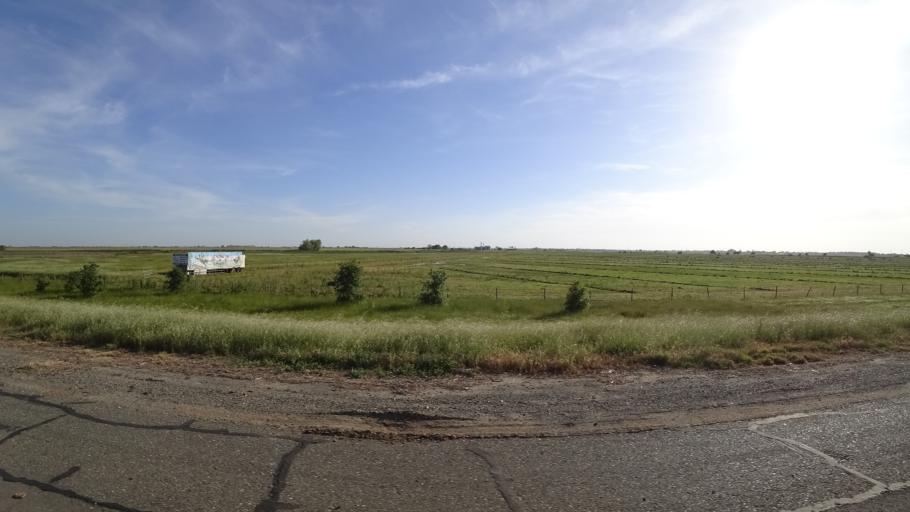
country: US
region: California
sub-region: Yuba County
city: Olivehurst
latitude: 39.0604
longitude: -121.5078
